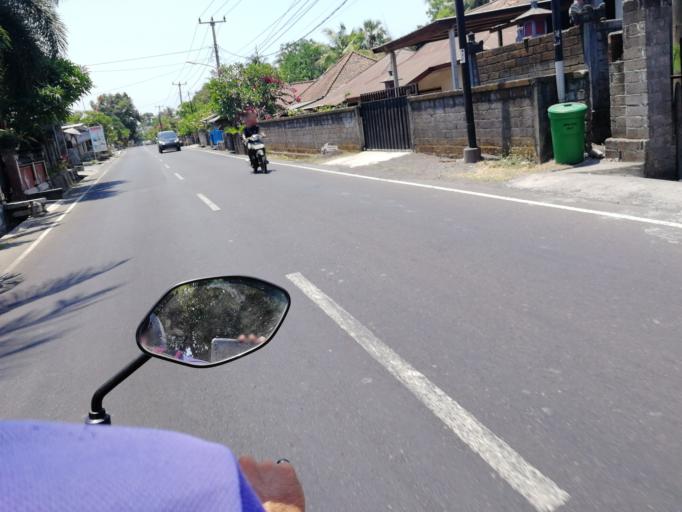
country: ID
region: Bali
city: Banjar Trunyan
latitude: -8.1424
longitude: 115.3922
